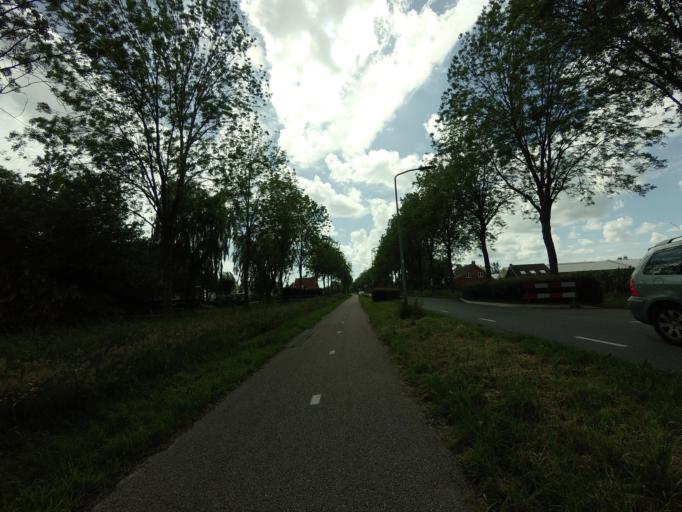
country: NL
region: North Holland
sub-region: Gemeente Hoorn
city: Hoorn
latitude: 52.6821
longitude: 5.0737
